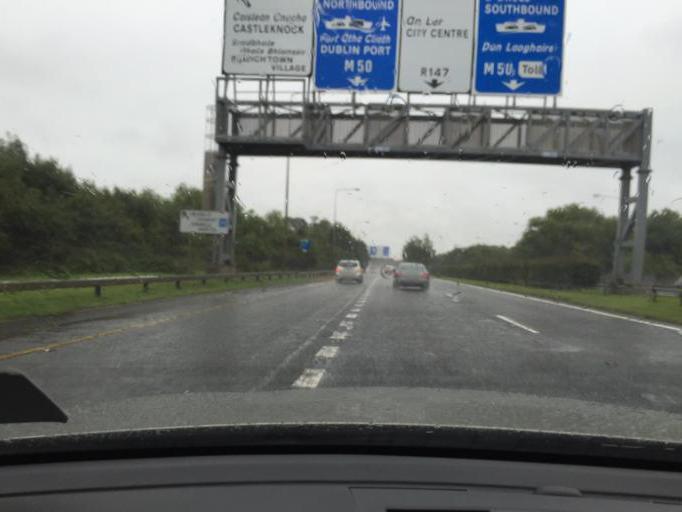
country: IE
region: Leinster
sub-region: Fingal County
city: Blanchardstown
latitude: 53.3888
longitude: -6.3753
